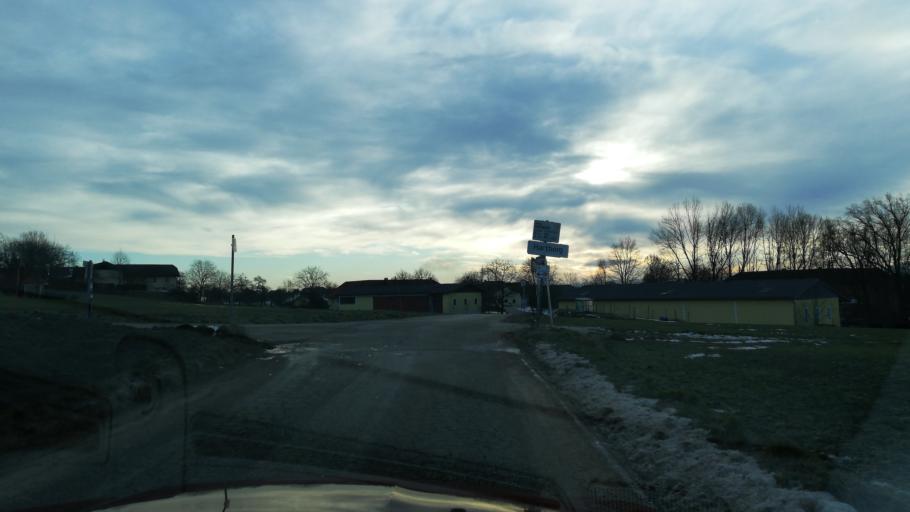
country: AT
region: Upper Austria
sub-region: Wels-Land
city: Buchkirchen
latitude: 48.2338
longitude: 13.9963
